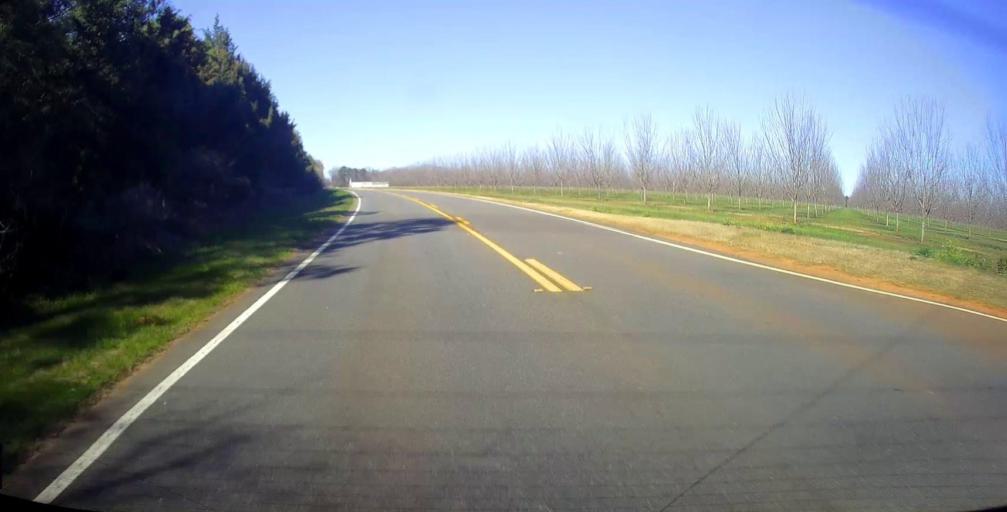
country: US
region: Georgia
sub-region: Macon County
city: Montezuma
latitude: 32.3671
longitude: -84.0131
